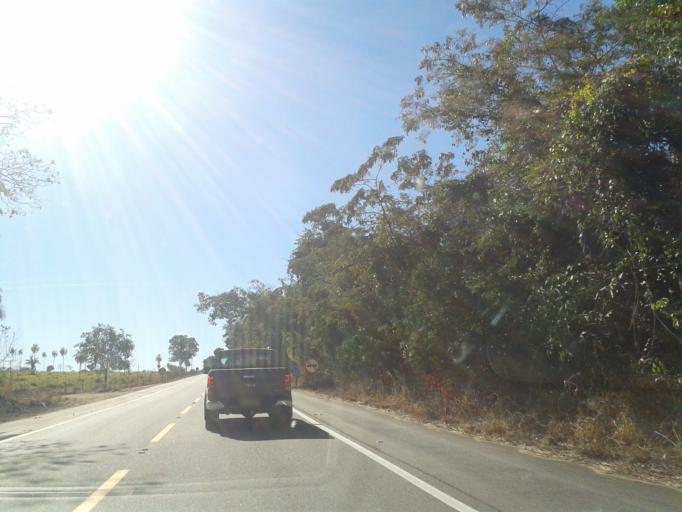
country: BR
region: Goias
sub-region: Itapuranga
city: Itapuranga
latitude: -15.5955
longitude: -50.2570
